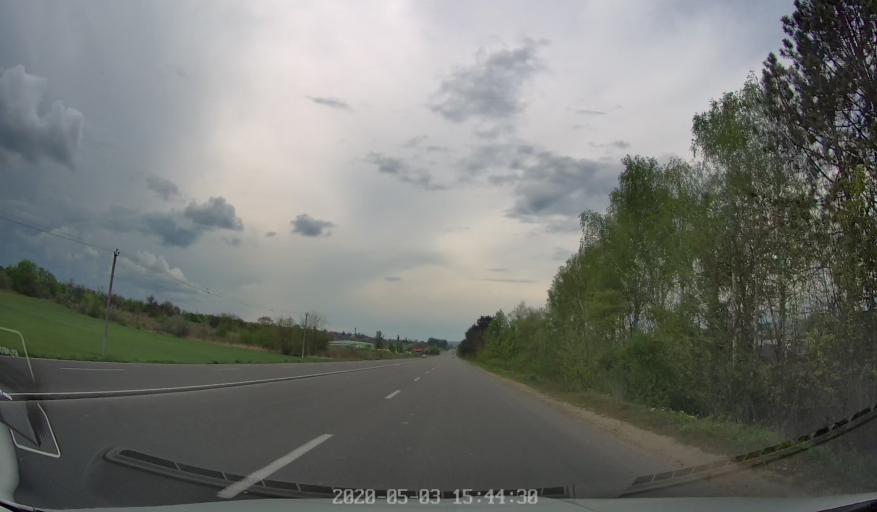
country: MD
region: Straseni
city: Straseni
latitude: 47.1331
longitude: 28.6544
